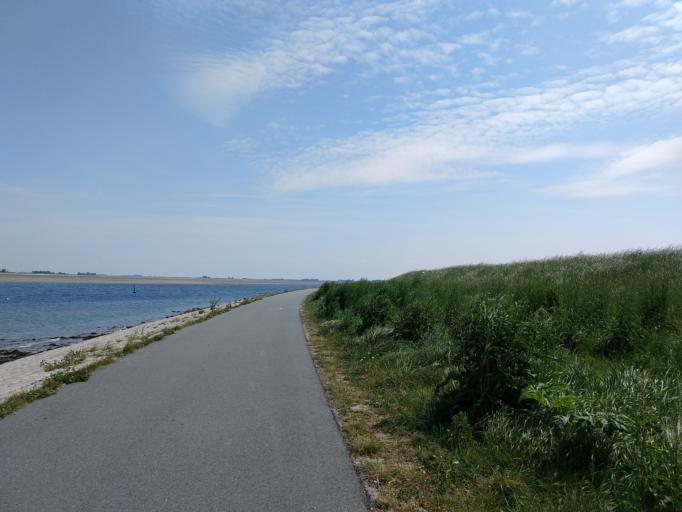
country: NL
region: Zeeland
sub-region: Schouwen-Duiveland
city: Bruinisse
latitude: 51.6105
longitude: 4.1000
